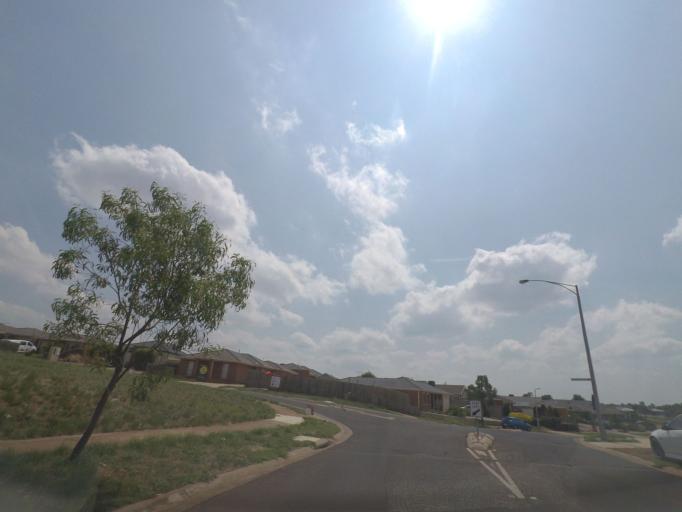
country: AU
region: Victoria
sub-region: Melton
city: Melton West
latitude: -37.6672
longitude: 144.5635
